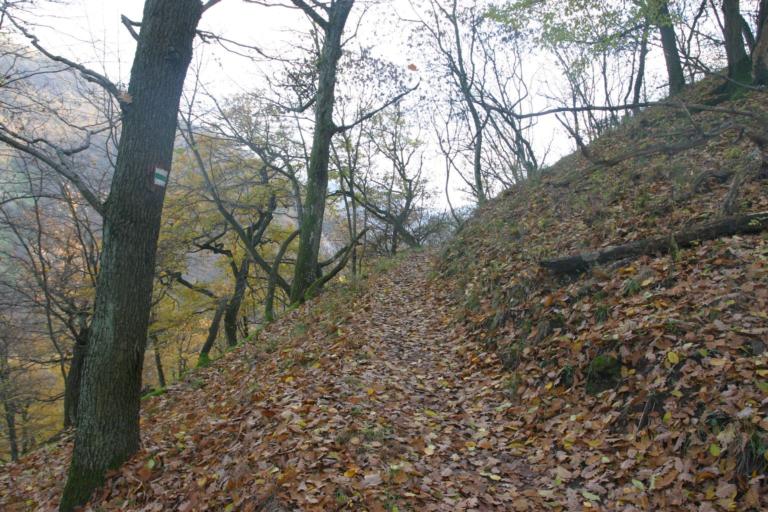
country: HU
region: Pest
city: Visegrad
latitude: 47.7613
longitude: 18.9790
